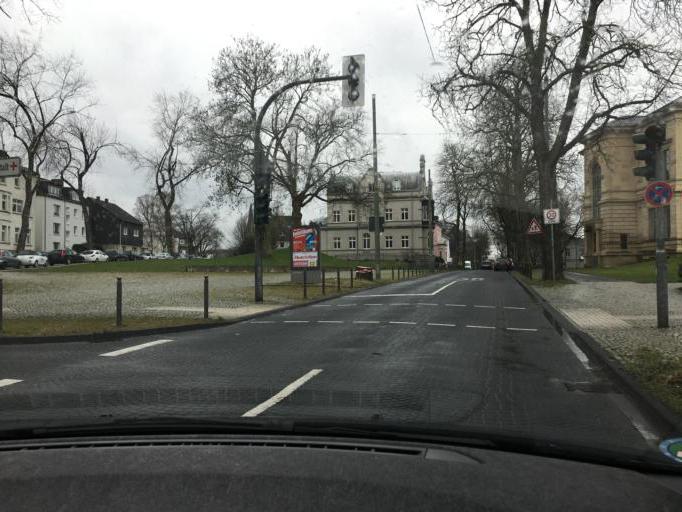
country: DE
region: North Rhine-Westphalia
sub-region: Regierungsbezirk Arnsberg
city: Bochum
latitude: 51.4873
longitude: 7.2216
